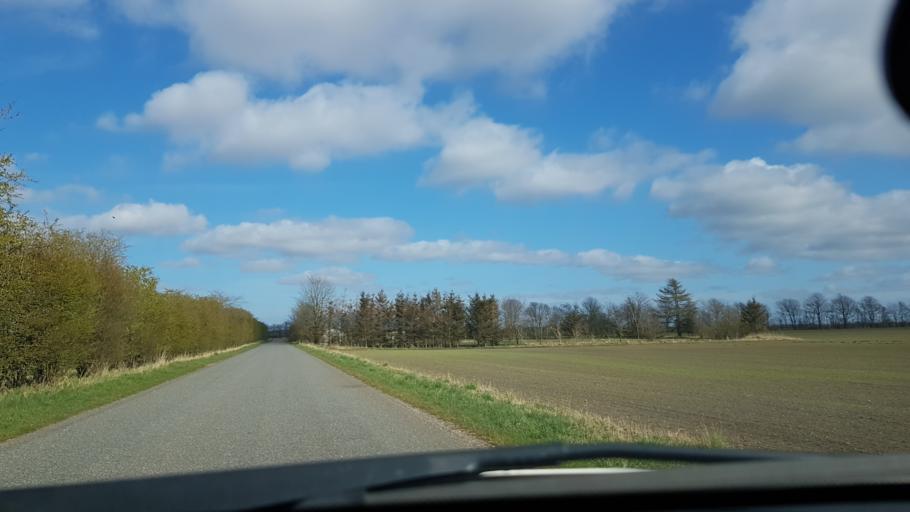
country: DK
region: South Denmark
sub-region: Vejen Kommune
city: Rodding
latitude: 55.3740
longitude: 8.9632
